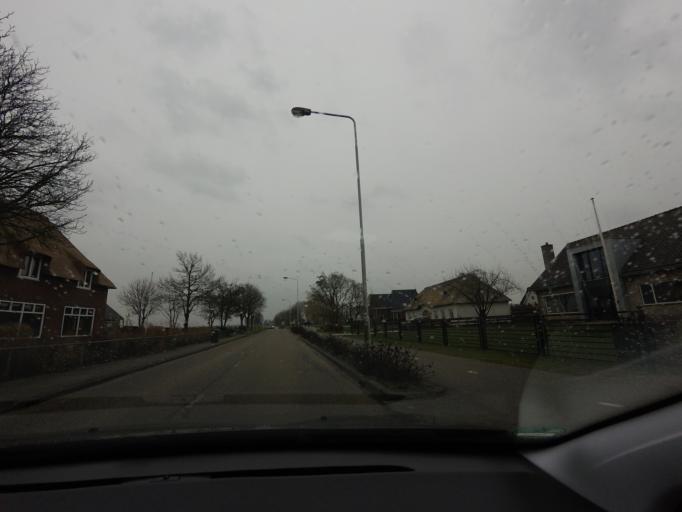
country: NL
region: Friesland
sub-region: Gemeente Franekeradeel
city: Franeker
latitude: 53.1813
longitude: 5.5539
